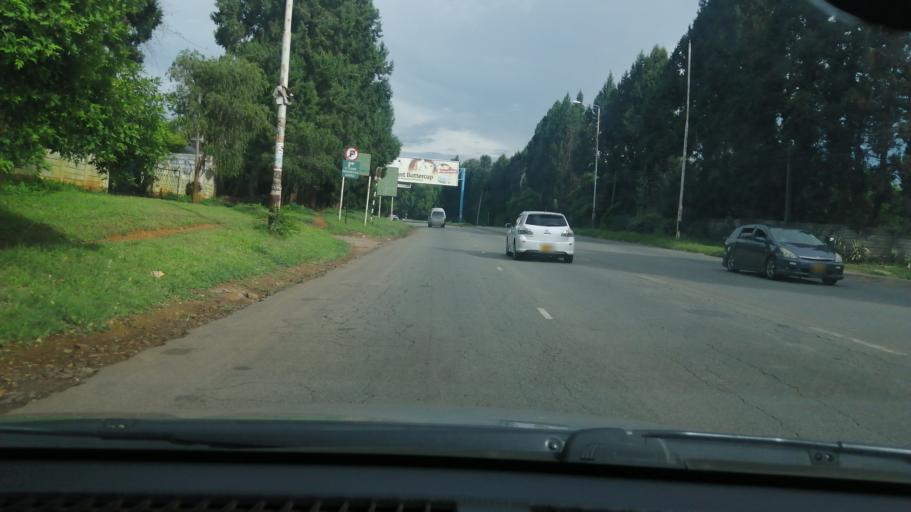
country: ZW
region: Harare
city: Harare
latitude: -17.7828
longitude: 31.0325
